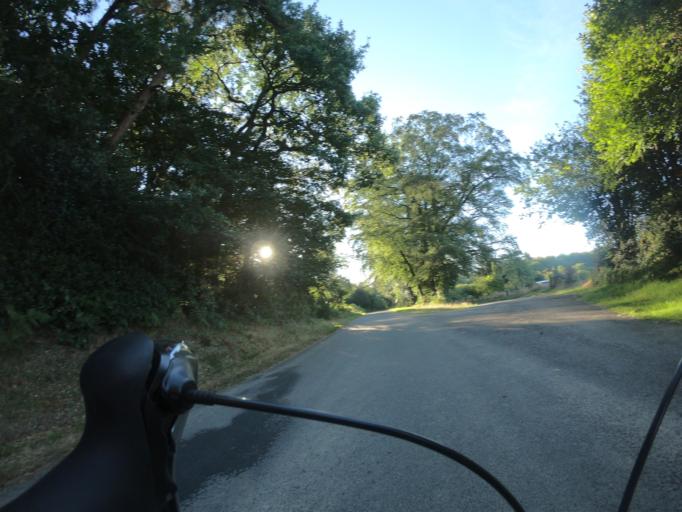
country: FR
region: Lower Normandy
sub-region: Departement de l'Orne
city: Magny-le-Desert
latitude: 48.5369
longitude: -0.2851
